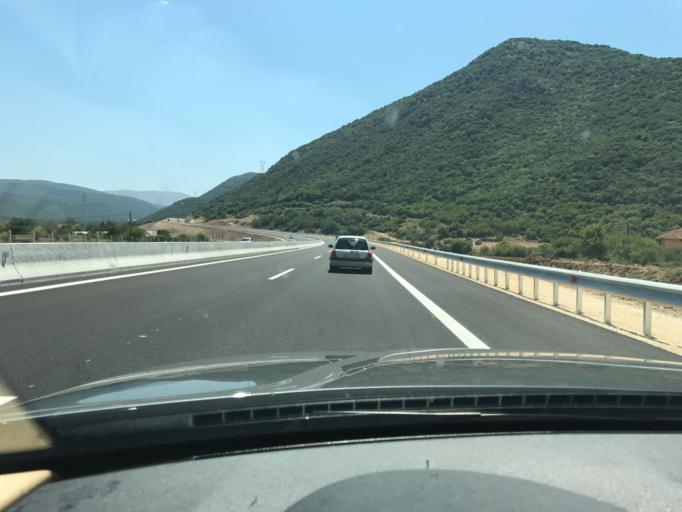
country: GR
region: Epirus
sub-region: Nomos Ioanninon
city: Agia Kyriaki
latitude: 39.5217
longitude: 20.8808
